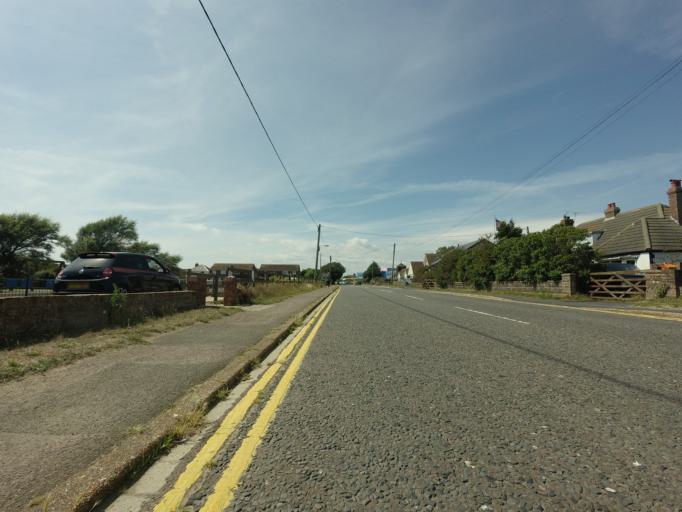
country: GB
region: England
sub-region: East Sussex
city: Rye
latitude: 50.9358
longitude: 0.7960
